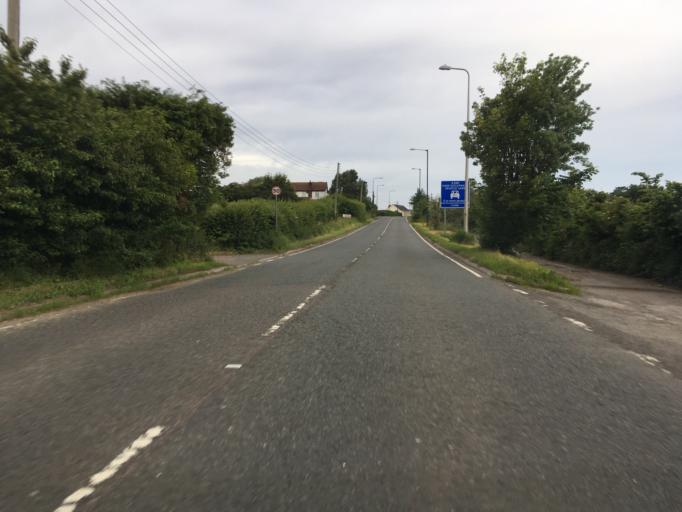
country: GB
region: England
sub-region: North Somerset
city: Easton-in-Gordano
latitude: 51.4714
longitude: -2.6919
